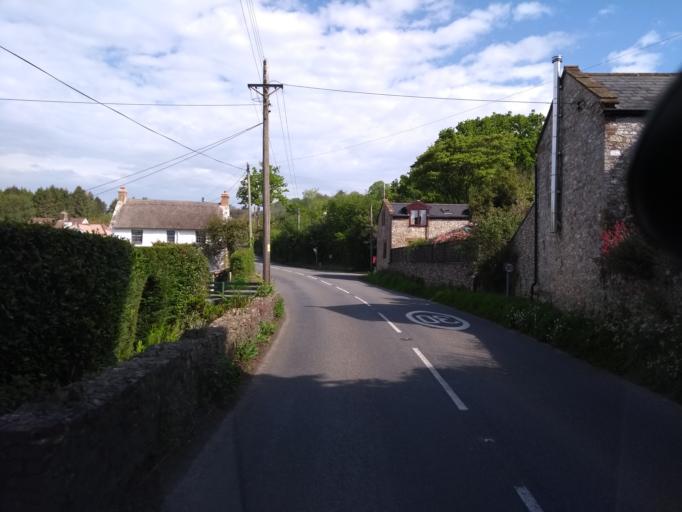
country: GB
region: England
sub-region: Dorset
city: Lyme Regis
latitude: 50.7443
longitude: -2.9657
